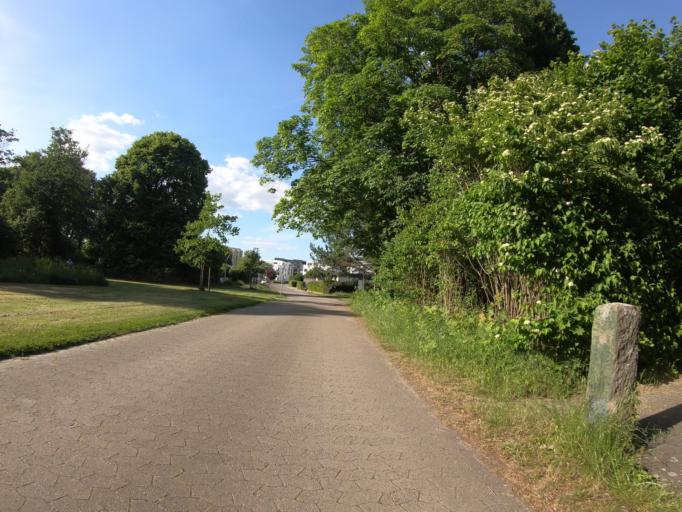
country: DE
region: Lower Saxony
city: Leiferde
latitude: 52.2236
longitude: 10.5385
